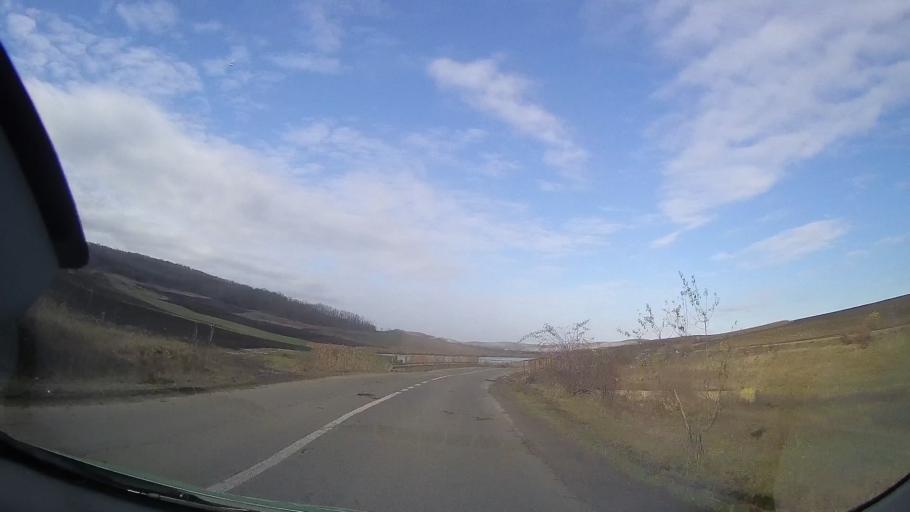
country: RO
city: Barza
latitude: 46.5553
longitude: 24.1006
